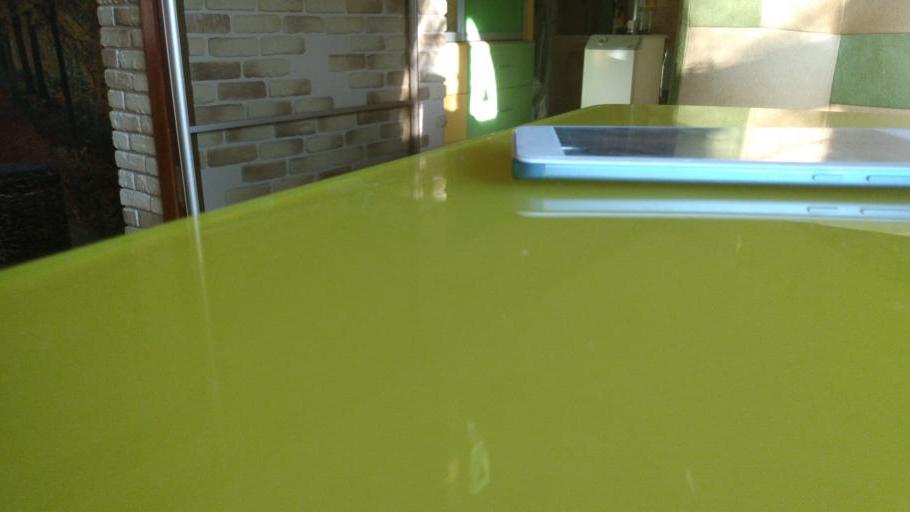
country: RU
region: Tverskaya
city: Vyshniy Volochek
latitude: 57.4525
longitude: 34.5701
